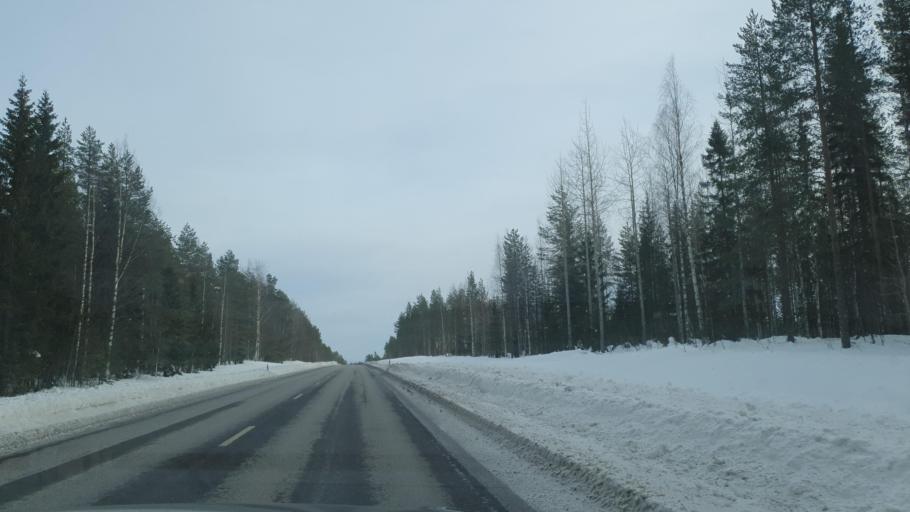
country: FI
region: Kainuu
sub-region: Kajaani
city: Vaala
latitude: 64.5504
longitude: 27.0664
